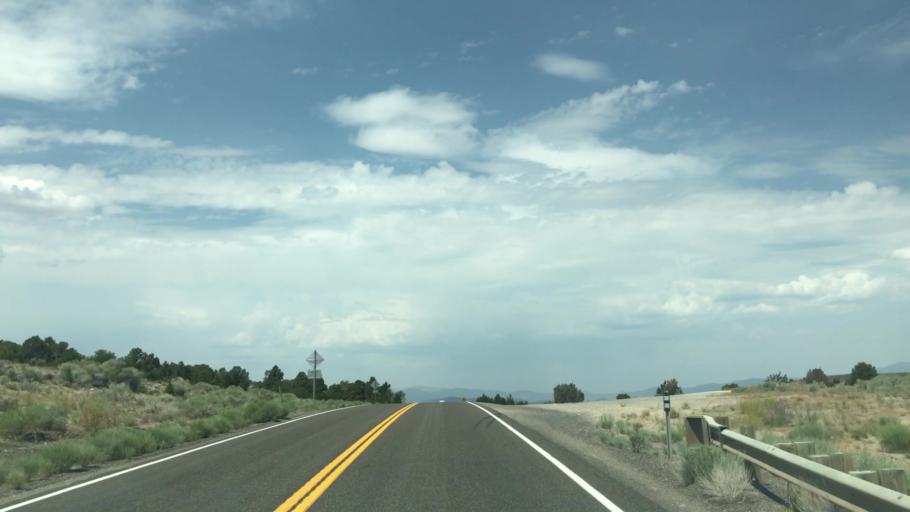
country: US
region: Nevada
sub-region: Eureka County
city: Eureka
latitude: 39.3913
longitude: -115.5040
